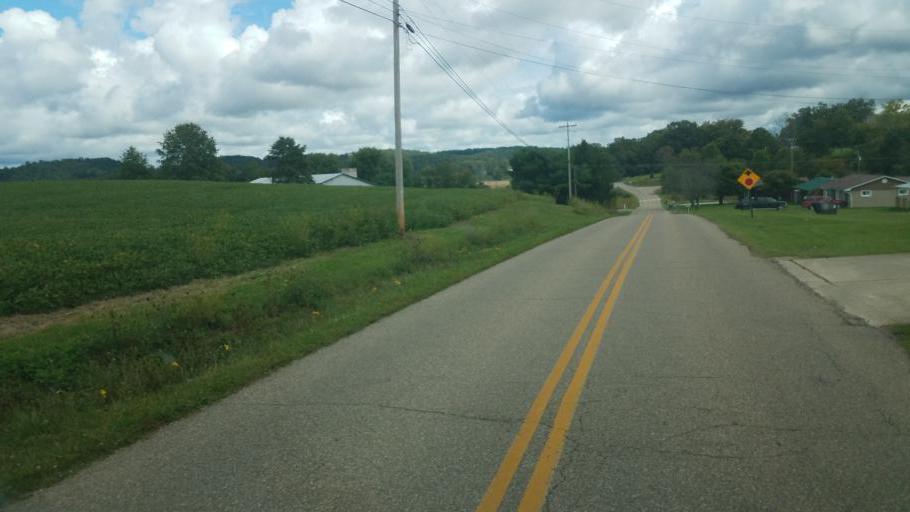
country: US
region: Ohio
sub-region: Scioto County
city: Sciotodale
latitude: 38.8667
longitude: -82.8579
